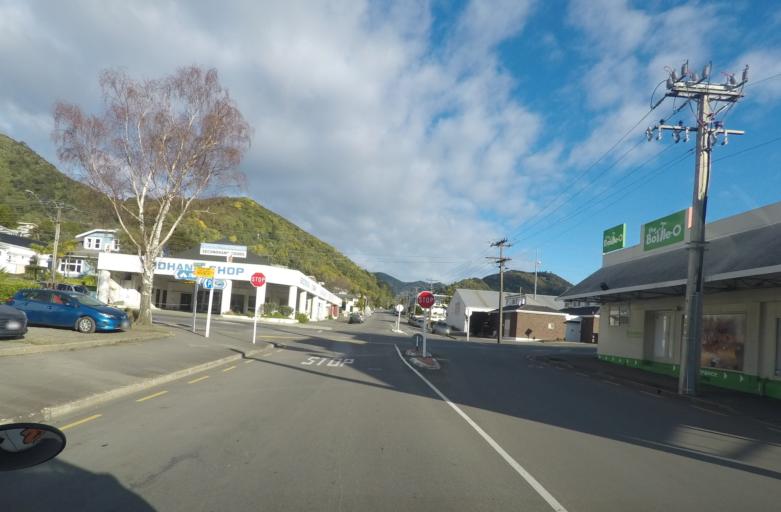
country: NZ
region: Marlborough
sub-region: Marlborough District
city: Picton
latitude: -41.2903
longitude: 174.0080
